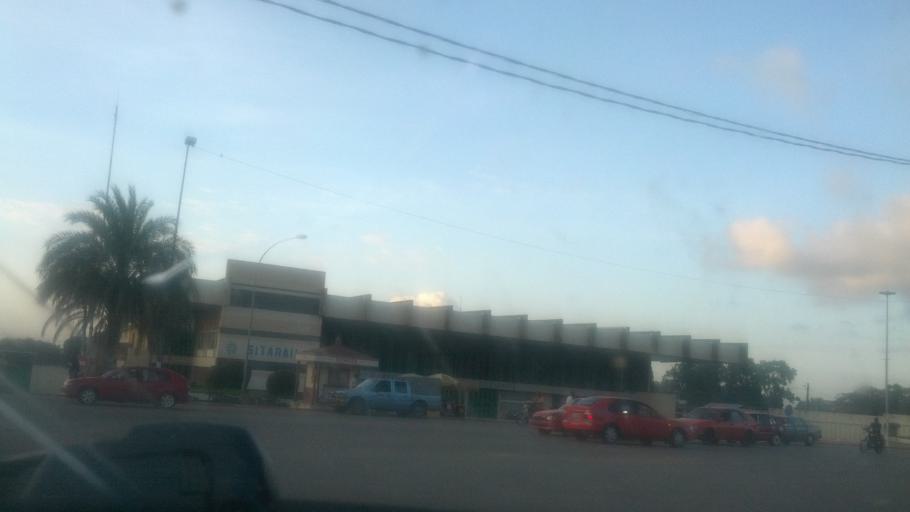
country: CI
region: Vallee du Bandama
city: Bouake
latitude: 7.6841
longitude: -5.0303
